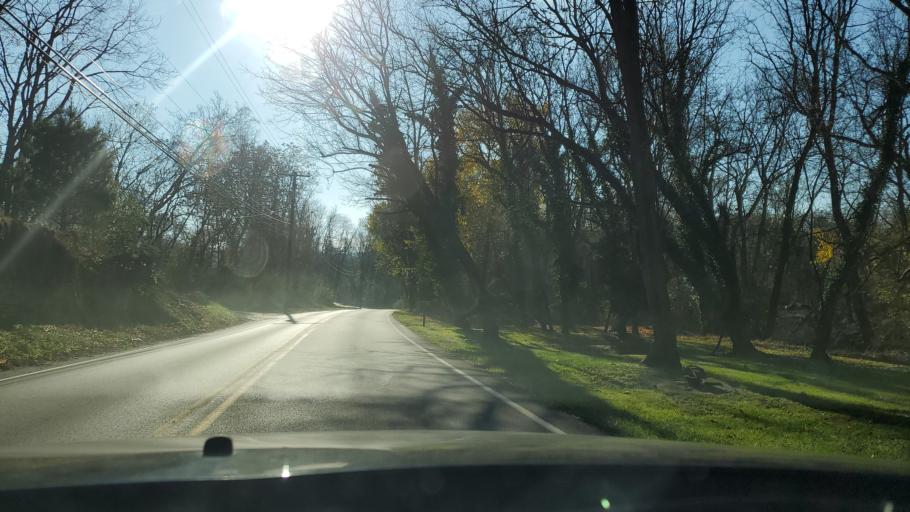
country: US
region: Pennsylvania
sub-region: Cumberland County
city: Mechanicsburg
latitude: 40.1671
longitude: -76.9849
